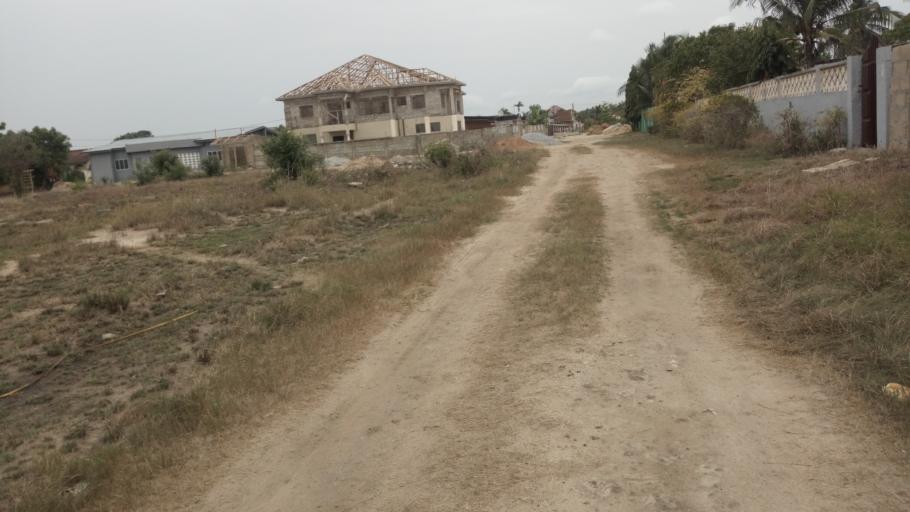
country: GH
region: Central
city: Winneba
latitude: 5.3637
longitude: -0.6389
